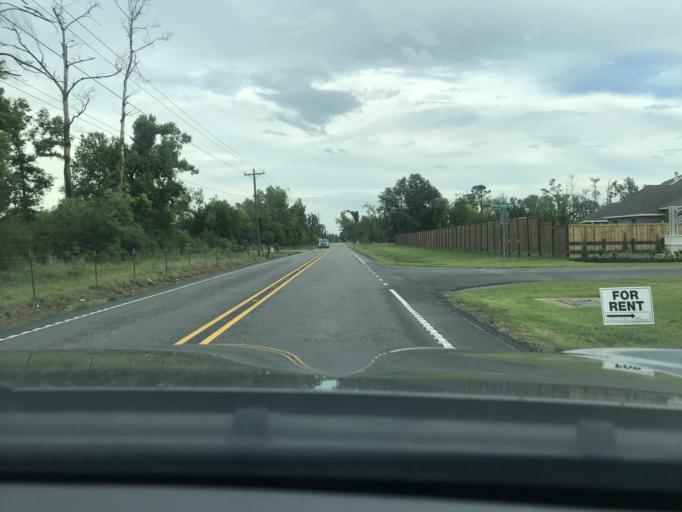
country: US
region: Louisiana
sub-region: Calcasieu Parish
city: Moss Bluff
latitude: 30.3127
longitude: -93.2583
